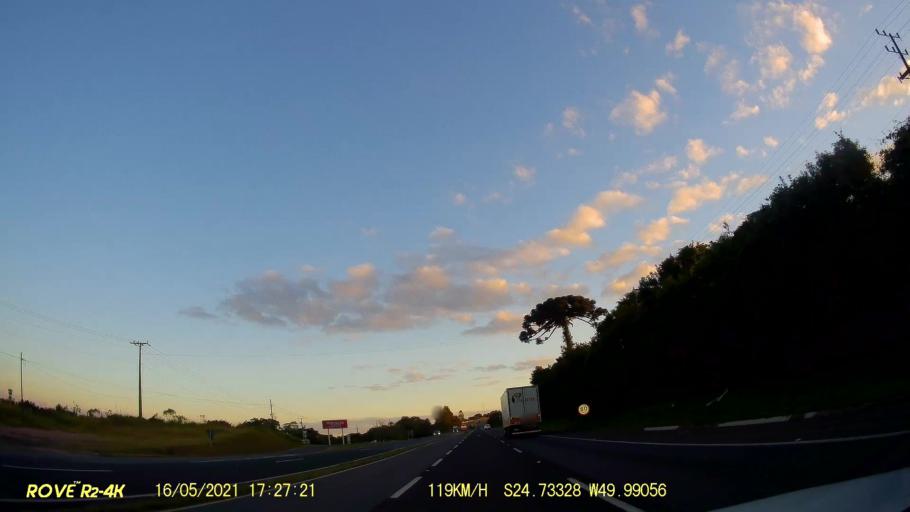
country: BR
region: Parana
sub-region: Castro
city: Castro
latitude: -24.7336
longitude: -49.9907
